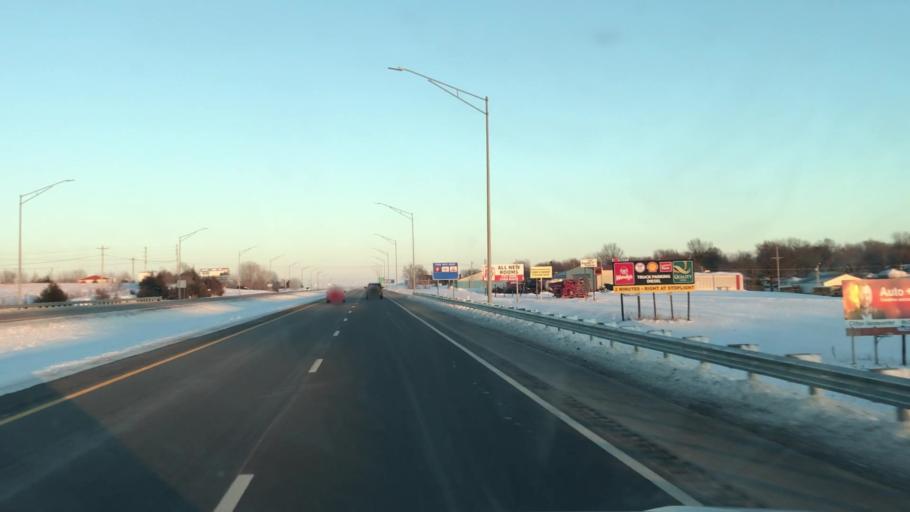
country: US
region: Missouri
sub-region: Clinton County
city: Cameron
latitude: 39.7541
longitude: -94.2470
